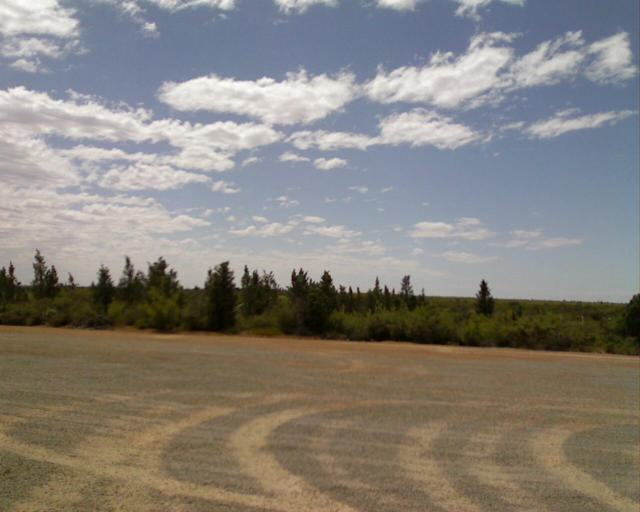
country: AU
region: Western Australia
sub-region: Moora
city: Moora
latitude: -30.0607
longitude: 115.6678
